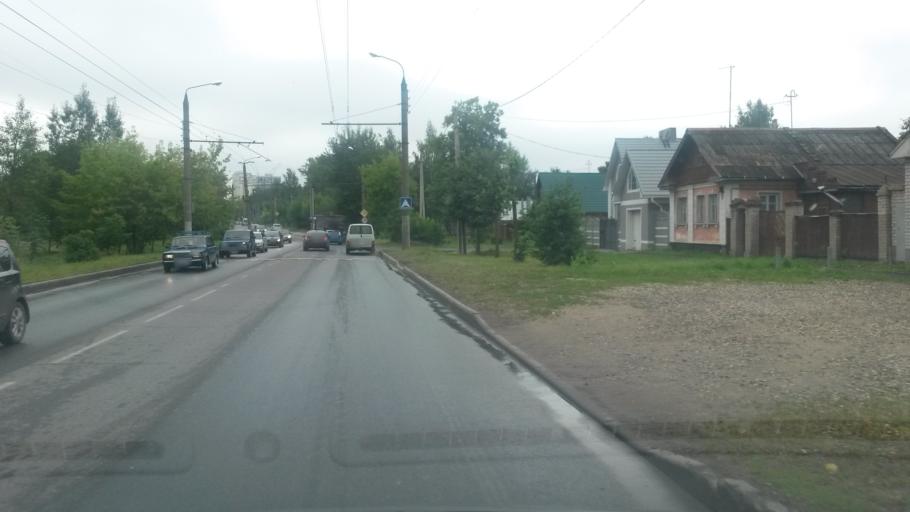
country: RU
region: Ivanovo
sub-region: Gorod Ivanovo
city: Ivanovo
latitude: 57.0114
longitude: 40.9383
